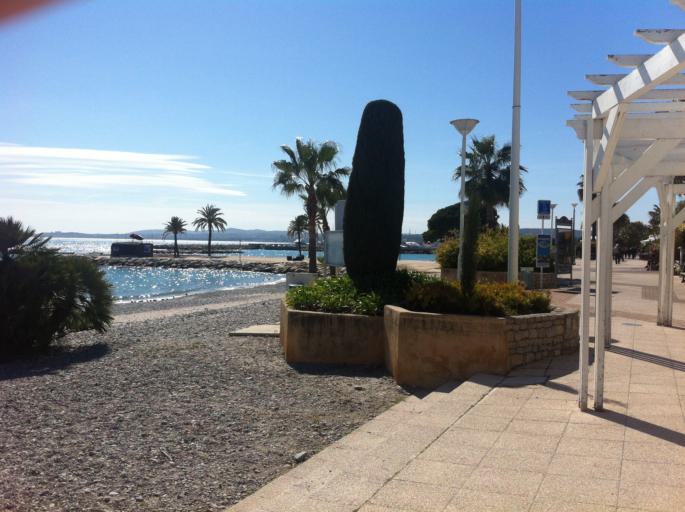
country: FR
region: Provence-Alpes-Cote d'Azur
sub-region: Departement des Alpes-Maritimes
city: Saint-Laurent-du-Var
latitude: 43.6579
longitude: 7.1902
